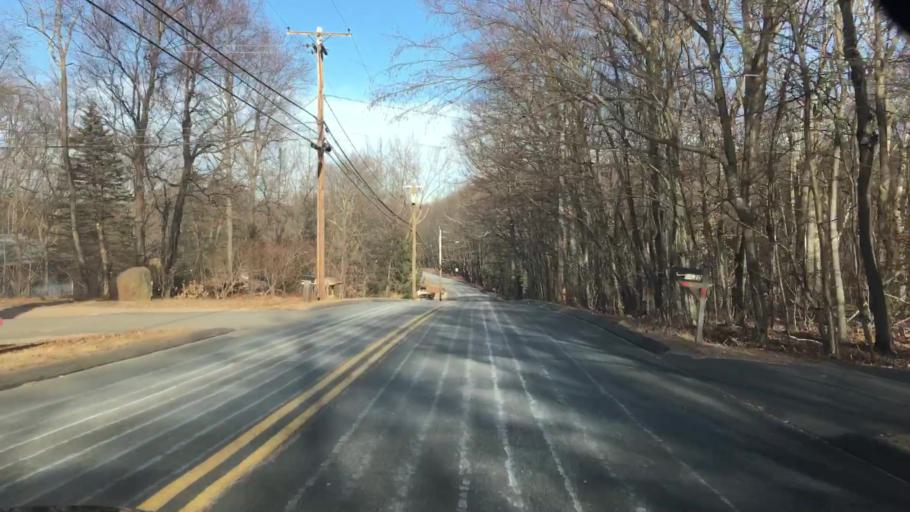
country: US
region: Connecticut
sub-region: New Haven County
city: Prospect
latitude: 41.5351
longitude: -72.9532
